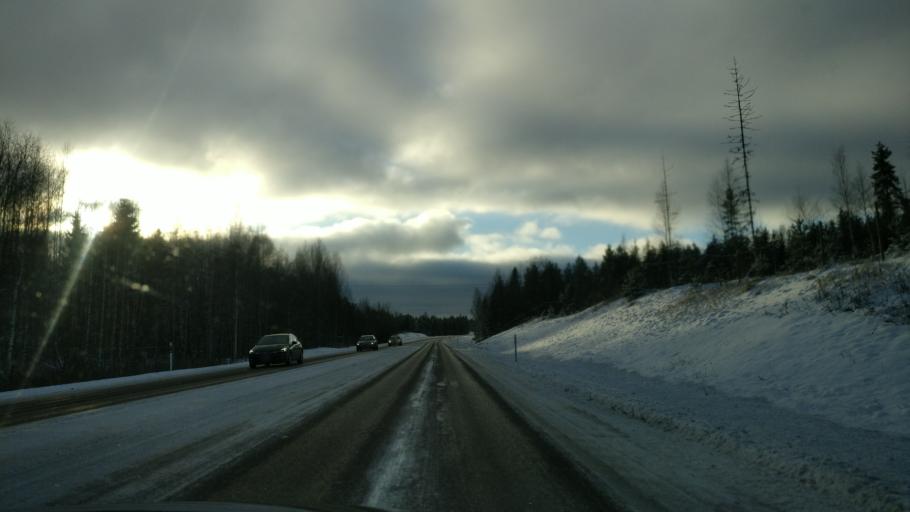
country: FI
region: Paijanne Tavastia
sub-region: Lahti
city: Heinola
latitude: 61.3533
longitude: 26.2238
